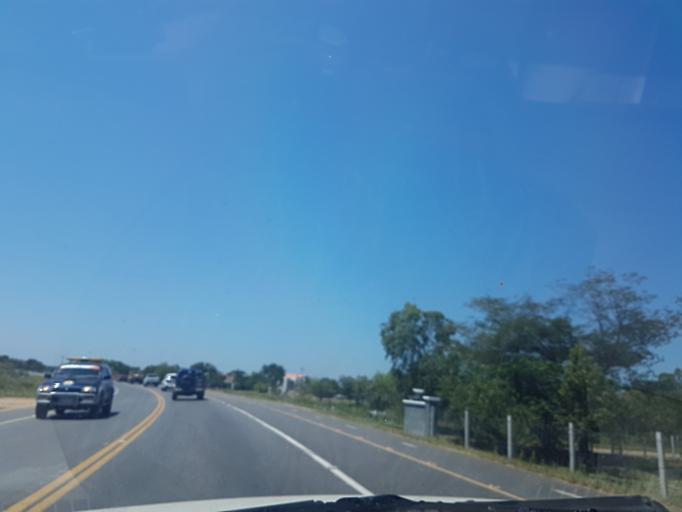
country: PY
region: Cordillera
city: San Bernardino
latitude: -25.2671
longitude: -57.3222
